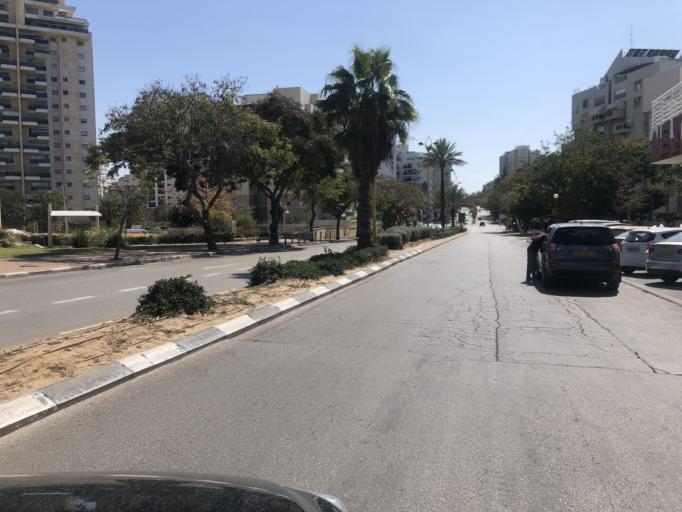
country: IL
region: Tel Aviv
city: Holon
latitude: 32.0029
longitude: 34.7677
